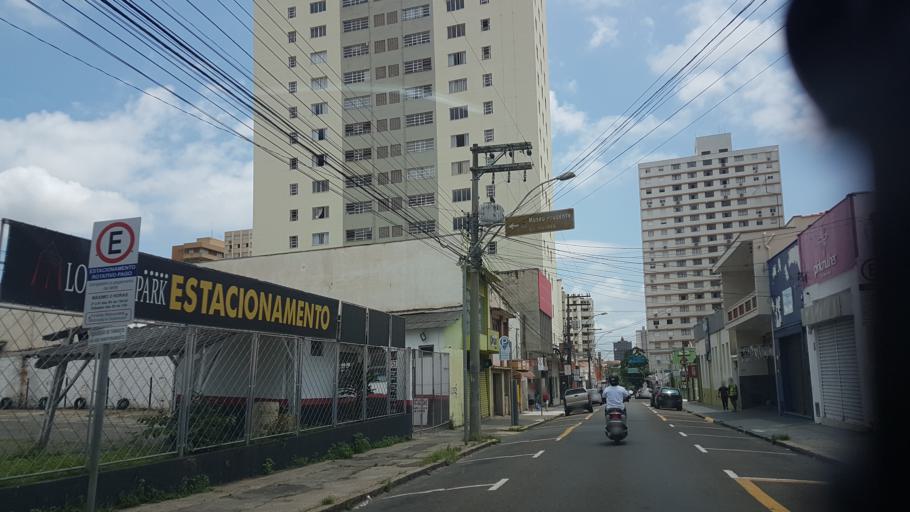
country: BR
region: Sao Paulo
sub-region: Piracicaba
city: Piracicaba
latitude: -22.7240
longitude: -47.6470
